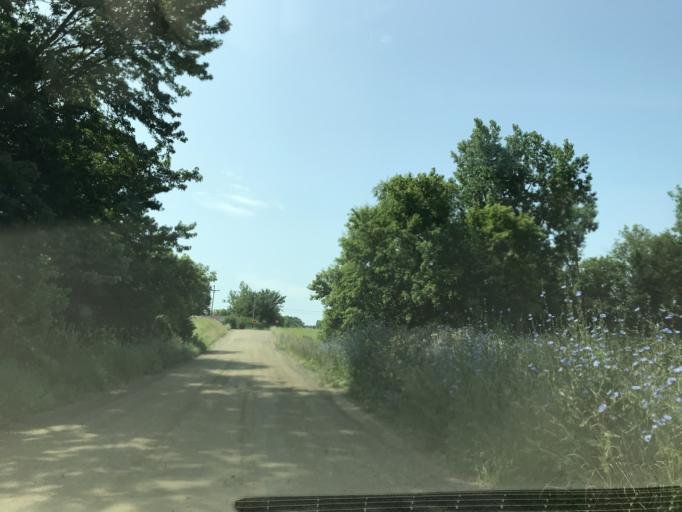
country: US
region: Michigan
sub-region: Eaton County
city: Grand Ledge
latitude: 42.7715
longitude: -84.7198
